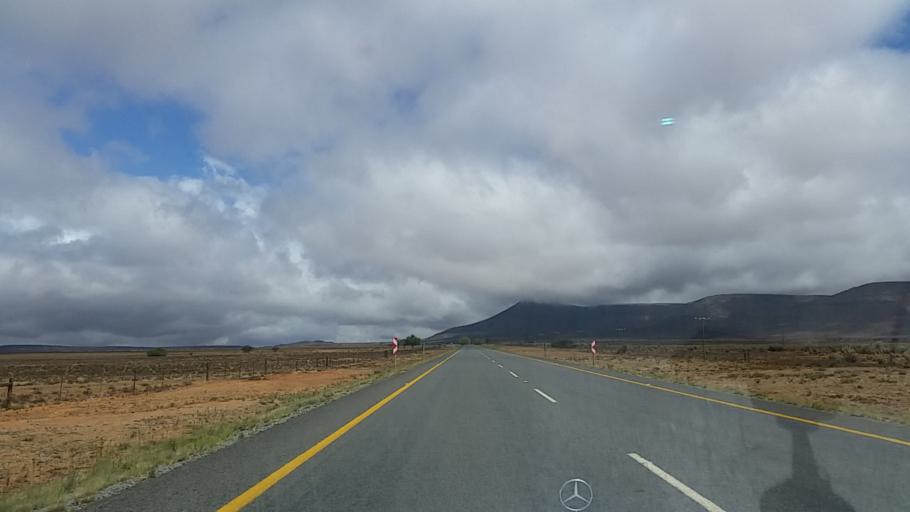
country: ZA
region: Eastern Cape
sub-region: Cacadu District Municipality
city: Graaff-Reinet
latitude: -32.0180
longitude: 24.6423
